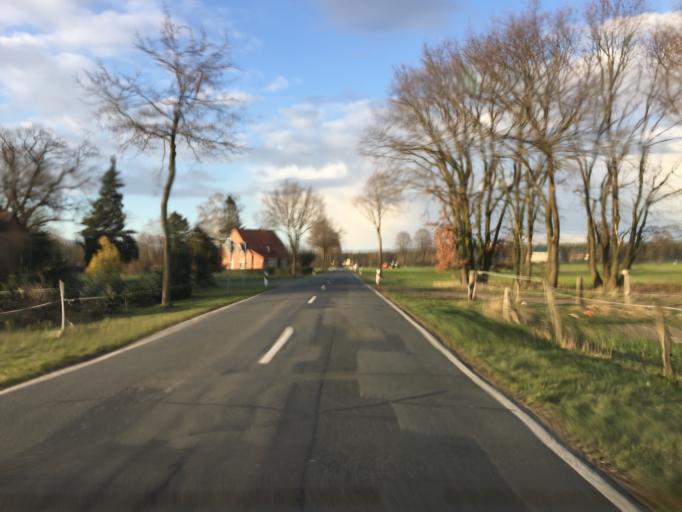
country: DE
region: Lower Saxony
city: Steyerberg
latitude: 52.5886
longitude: 8.9800
